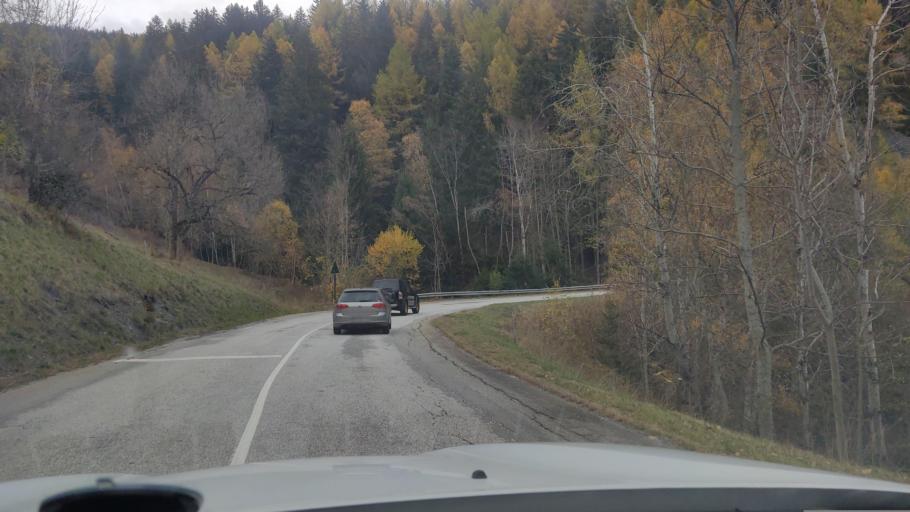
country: FR
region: Rhone-Alpes
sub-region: Departement de la Savoie
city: Bourg-Saint-Maurice
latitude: 45.6023
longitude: 6.7833
